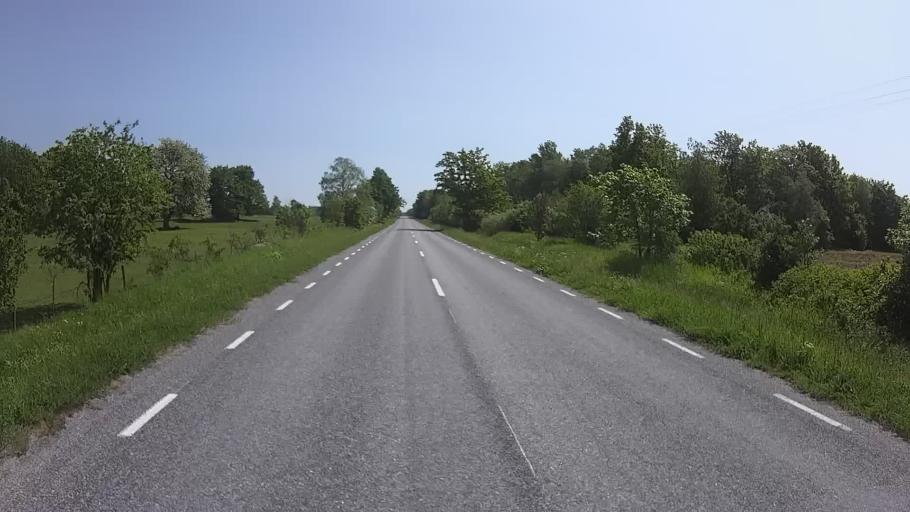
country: EE
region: Saare
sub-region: Kuressaare linn
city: Kuressaare
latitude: 58.3680
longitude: 22.0502
